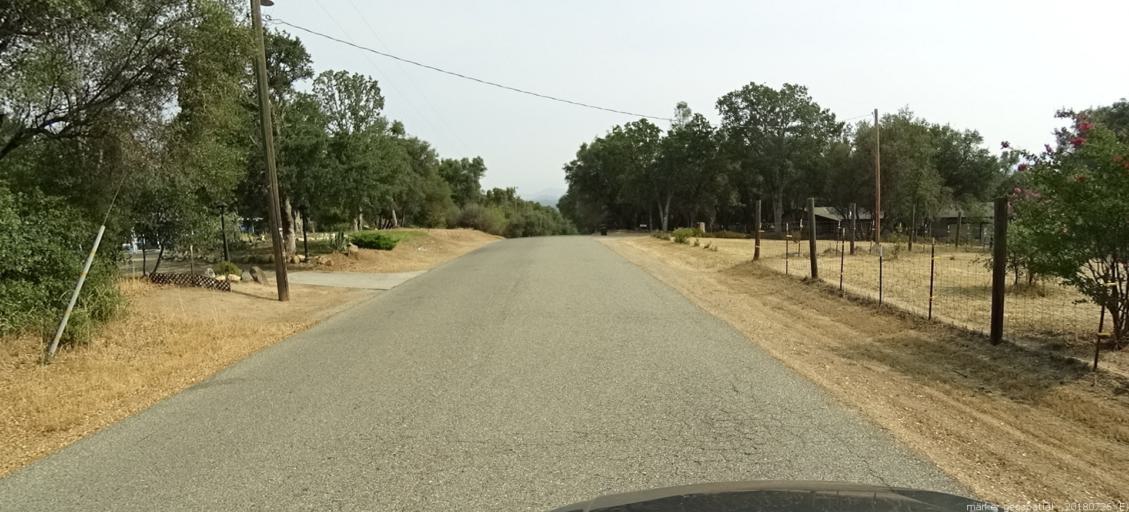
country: US
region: California
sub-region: Madera County
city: Coarsegold
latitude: 37.2131
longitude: -119.6897
